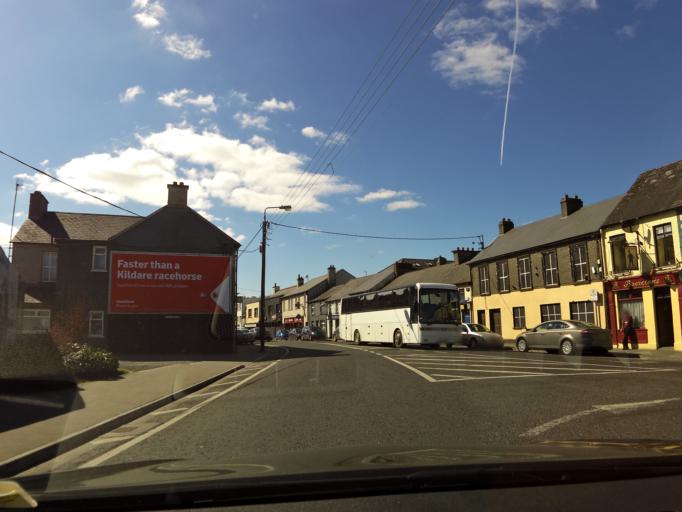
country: IE
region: Leinster
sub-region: Kildare
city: Athy
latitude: 52.9927
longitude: -6.9798
